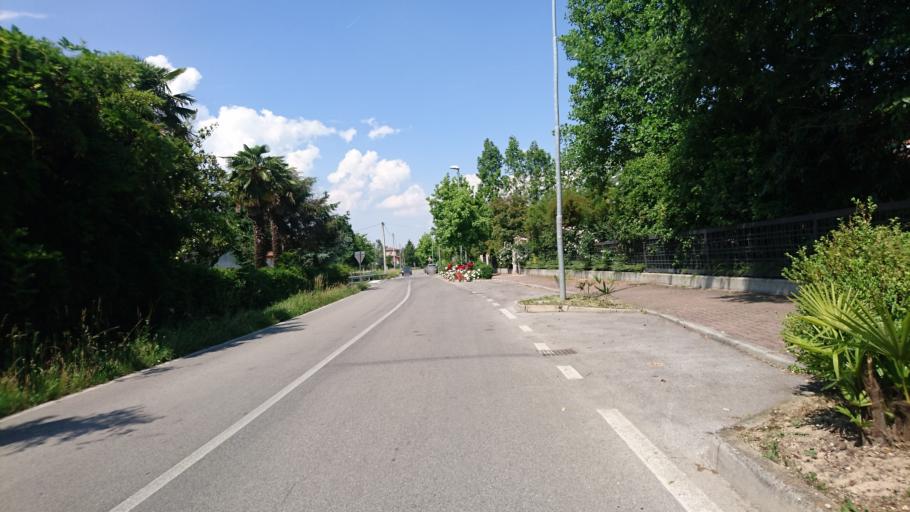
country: IT
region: Veneto
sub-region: Provincia di Padova
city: Masera di Padova
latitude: 45.2996
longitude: 11.8511
